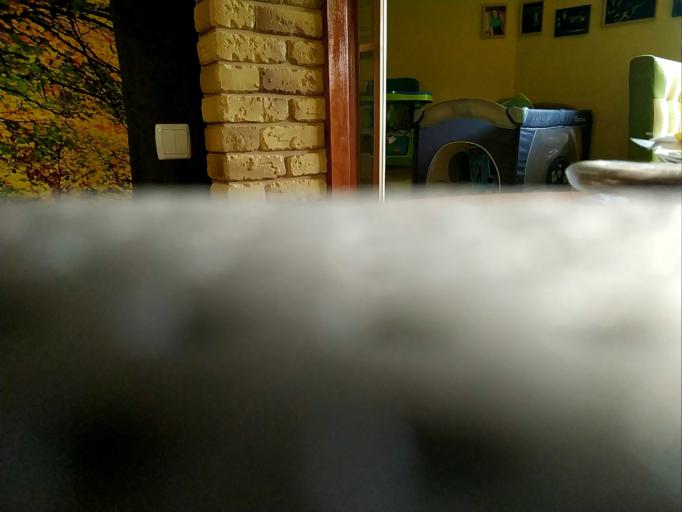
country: RU
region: Kaluga
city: Seredeyskiy
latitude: 53.9149
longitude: 35.3498
